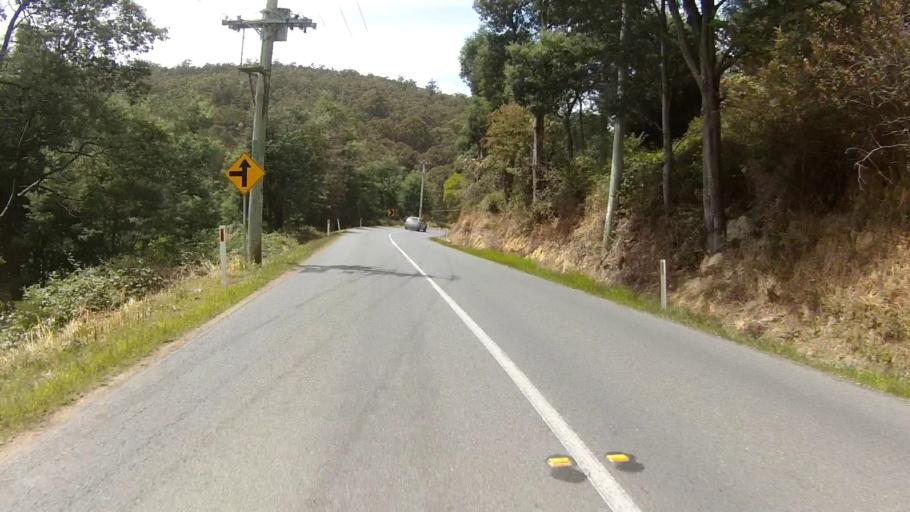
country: AU
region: Tasmania
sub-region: Kingborough
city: Kettering
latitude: -43.1041
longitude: 147.2231
